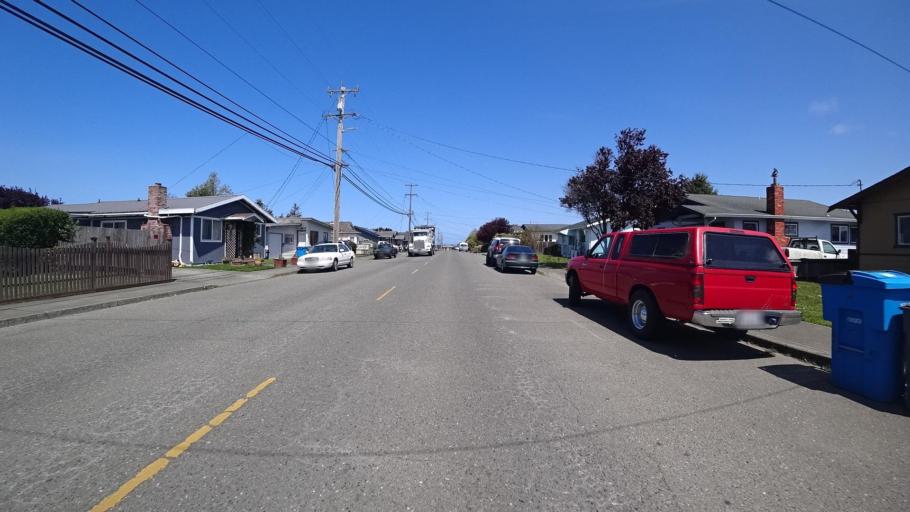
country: US
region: California
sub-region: Humboldt County
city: Bayview
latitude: 40.7773
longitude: -124.1749
